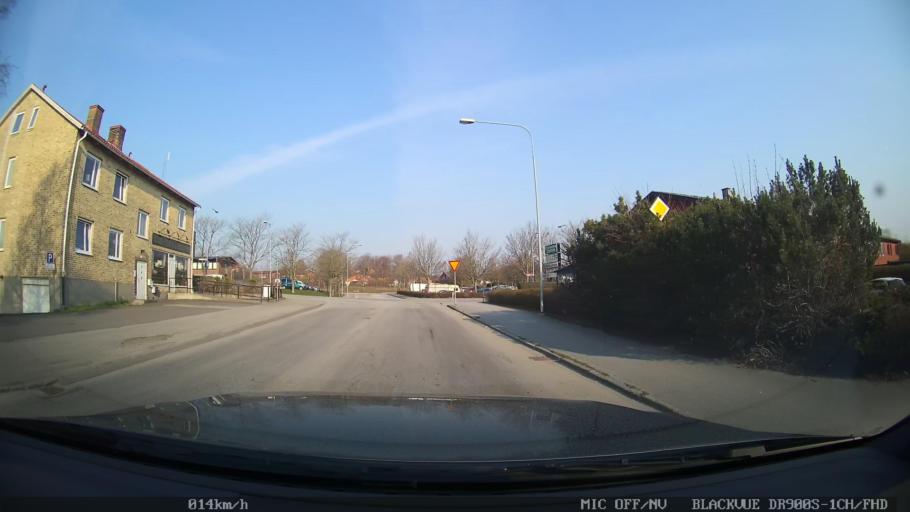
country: SE
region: Skane
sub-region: Ystads Kommun
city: Ystad
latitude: 55.4393
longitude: 13.8296
